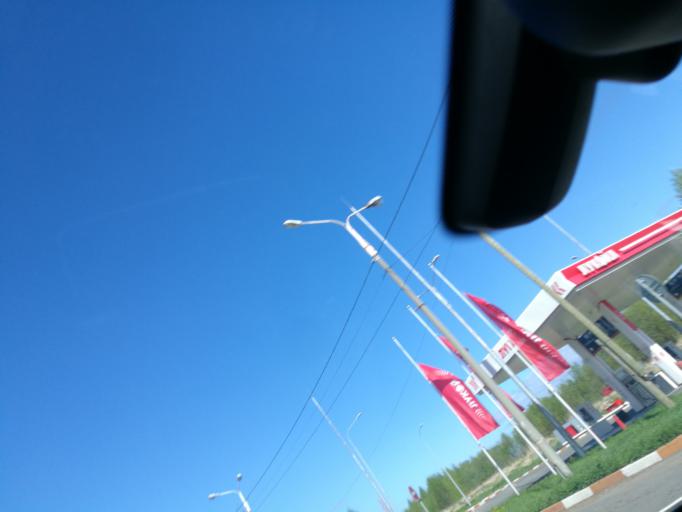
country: RU
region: Arkhangelskaya
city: Arkhangel'sk
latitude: 64.5976
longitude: 40.5609
